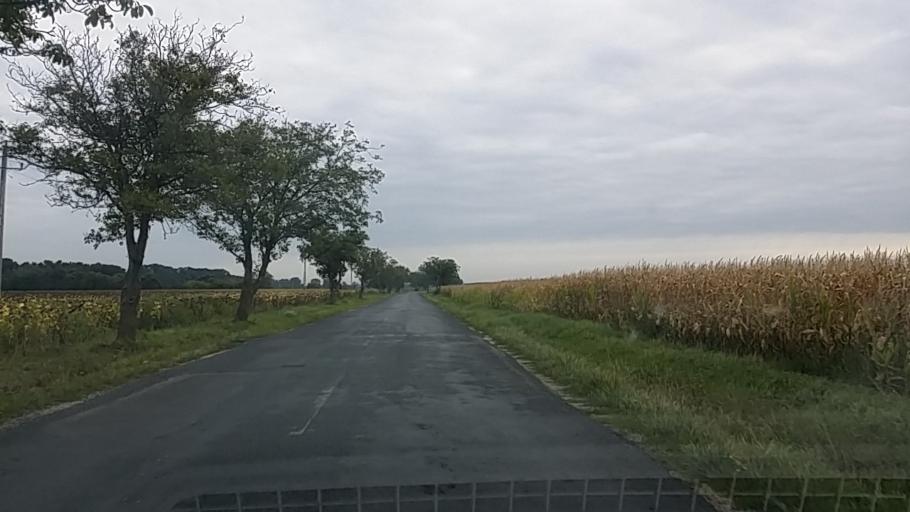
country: HU
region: Gyor-Moson-Sopron
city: Kapuvar
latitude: 47.6176
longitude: 17.0634
